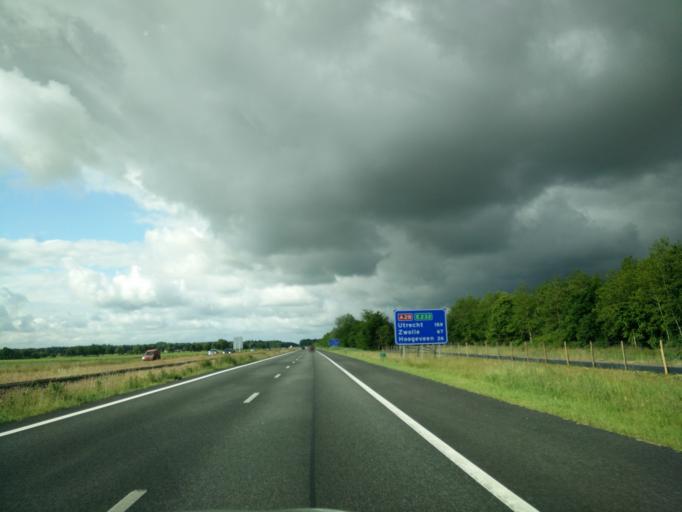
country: NL
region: Drenthe
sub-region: Gemeente Assen
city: Assen
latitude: 52.9424
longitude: 6.5390
